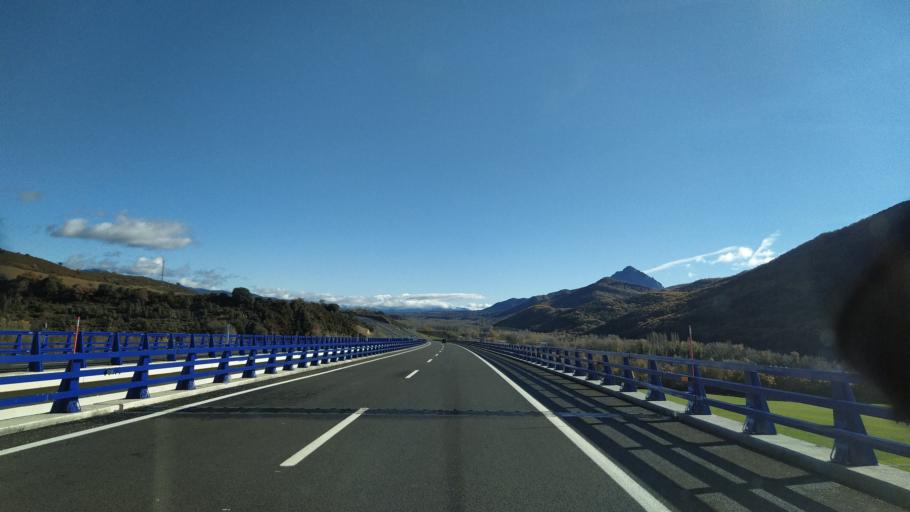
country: ES
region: Aragon
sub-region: Provincia de Huesca
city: Santa Cruz de la Seros
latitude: 42.5620
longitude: -0.6710
